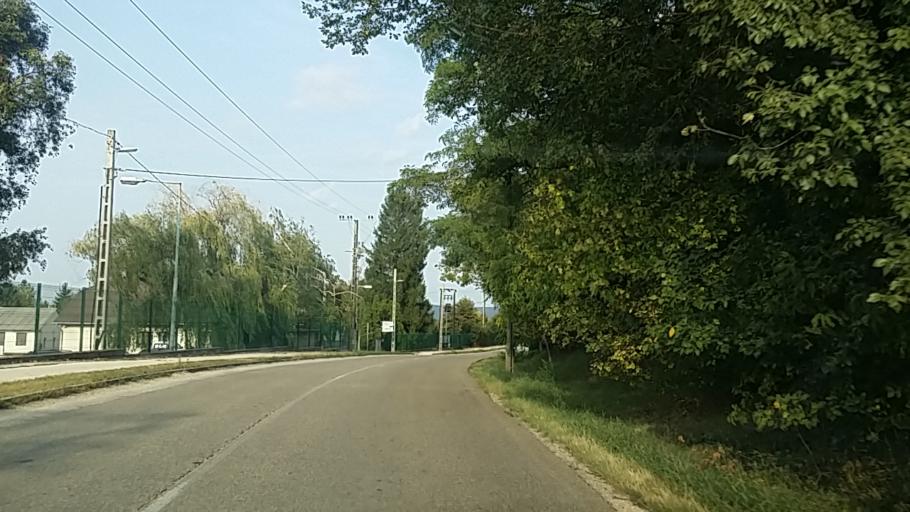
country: HU
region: Komarom-Esztergom
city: Tata
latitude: 47.6358
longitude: 18.2972
